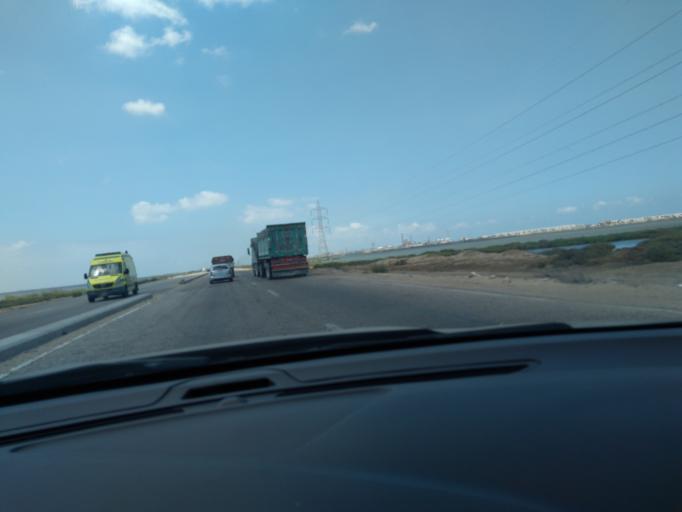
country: EG
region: Muhafazat Bur Sa`id
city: Port Said
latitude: 31.2819
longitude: 32.1879
